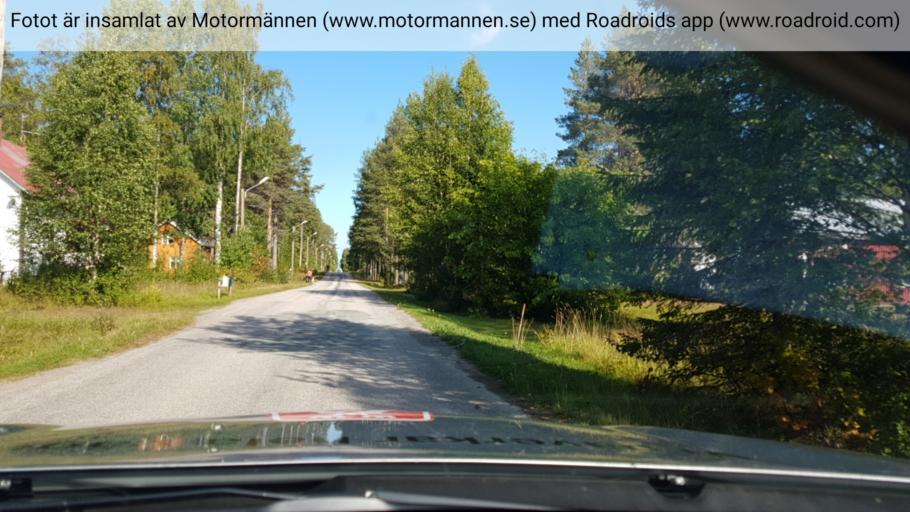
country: SE
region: Norrbotten
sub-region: Kalix Kommun
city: Kalix
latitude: 66.1730
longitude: 23.2162
